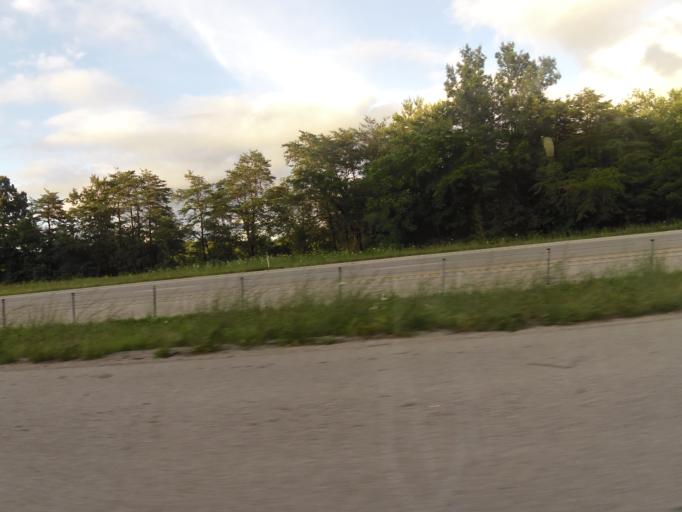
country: US
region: Kentucky
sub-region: Laurel County
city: London
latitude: 37.1602
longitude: -84.1138
